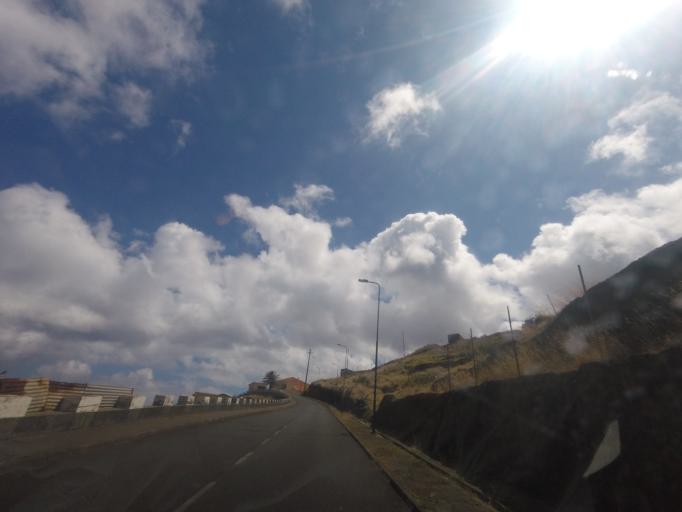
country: PT
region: Madeira
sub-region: Machico
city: Canical
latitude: 32.7456
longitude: -16.7411
